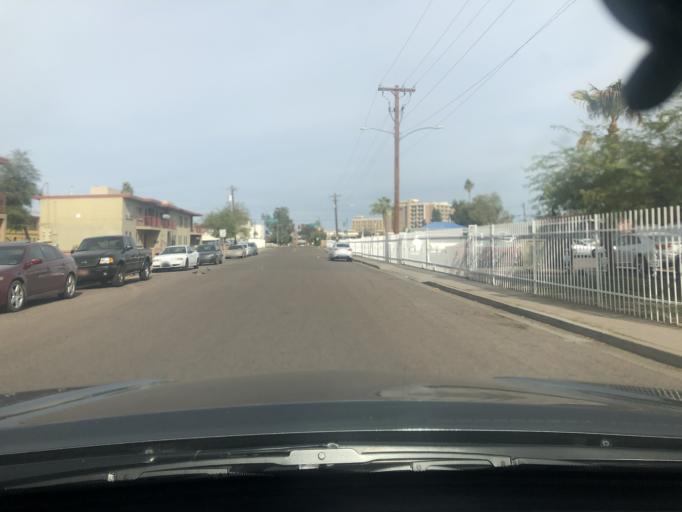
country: US
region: Arizona
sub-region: Maricopa County
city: Phoenix
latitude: 33.4500
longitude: -112.0434
